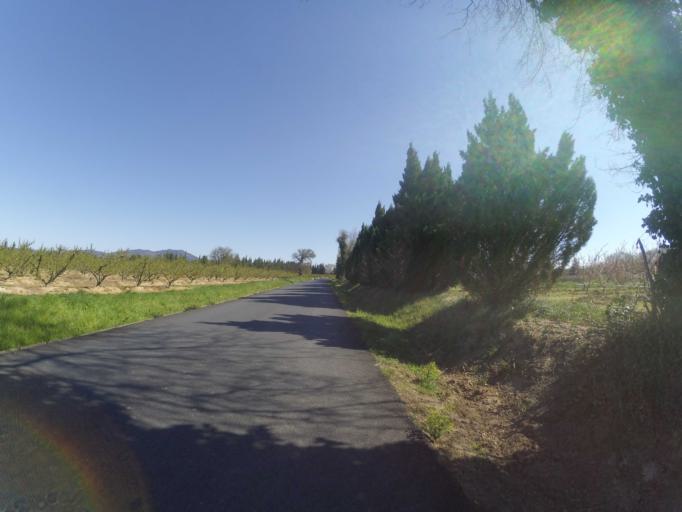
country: FR
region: Languedoc-Roussillon
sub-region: Departement des Pyrenees-Orientales
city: Millas
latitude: 42.6761
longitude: 2.6675
